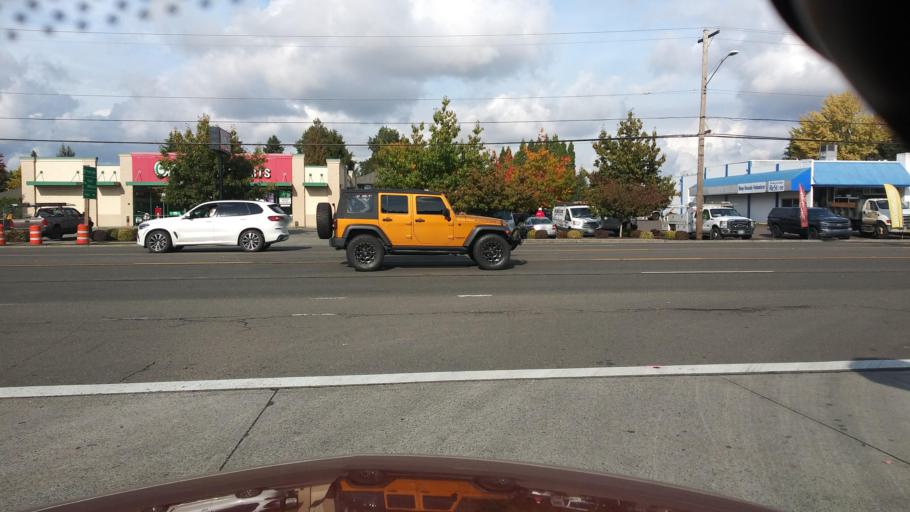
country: US
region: Oregon
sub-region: Washington County
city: Cornelius
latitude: 45.5200
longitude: -123.0818
